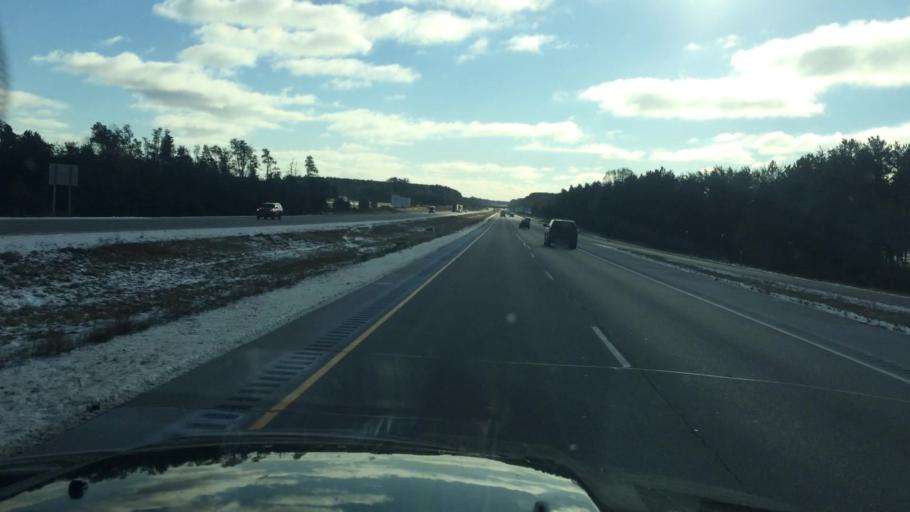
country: US
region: Wisconsin
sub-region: Portage County
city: Stevens Point
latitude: 44.5393
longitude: -89.5432
